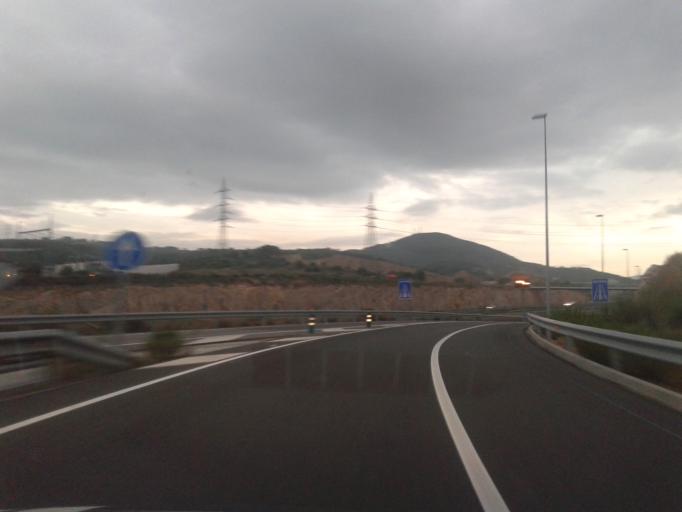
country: ES
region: Catalonia
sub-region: Provincia de Barcelona
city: Vilanova i la Geltru
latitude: 41.2526
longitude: 1.7192
